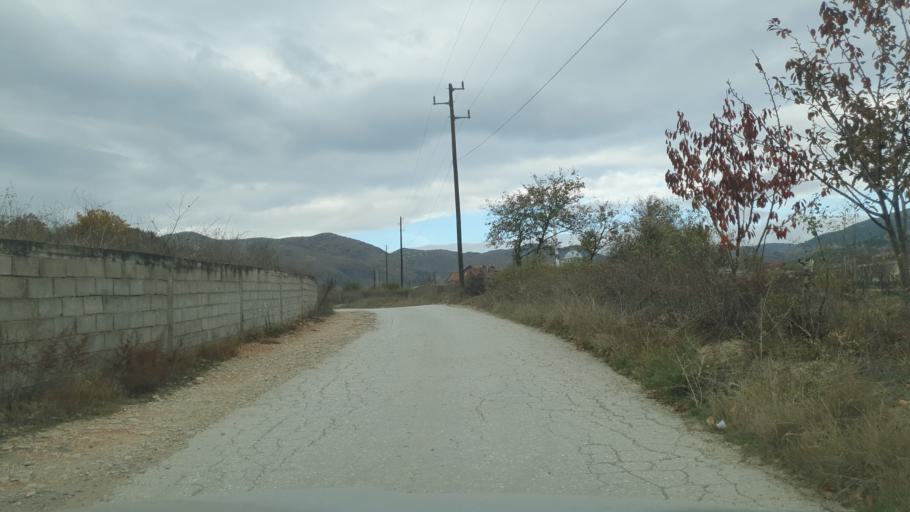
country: MK
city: Kondovo
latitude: 42.0389
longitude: 21.2801
